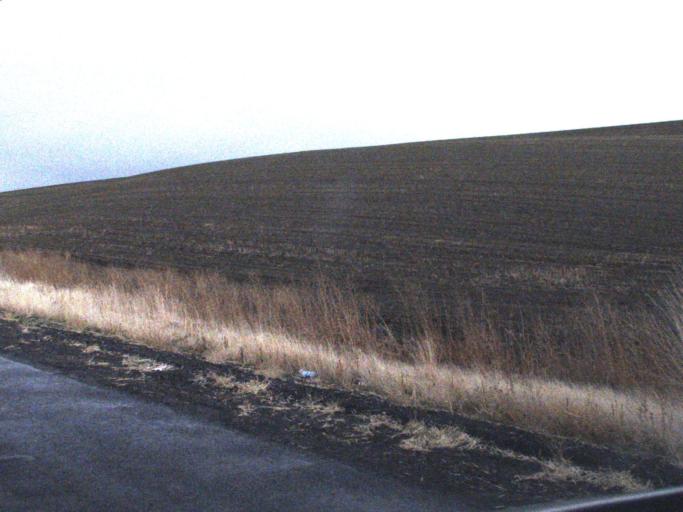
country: US
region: Washington
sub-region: Columbia County
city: Dayton
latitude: 46.3872
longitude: -117.9391
